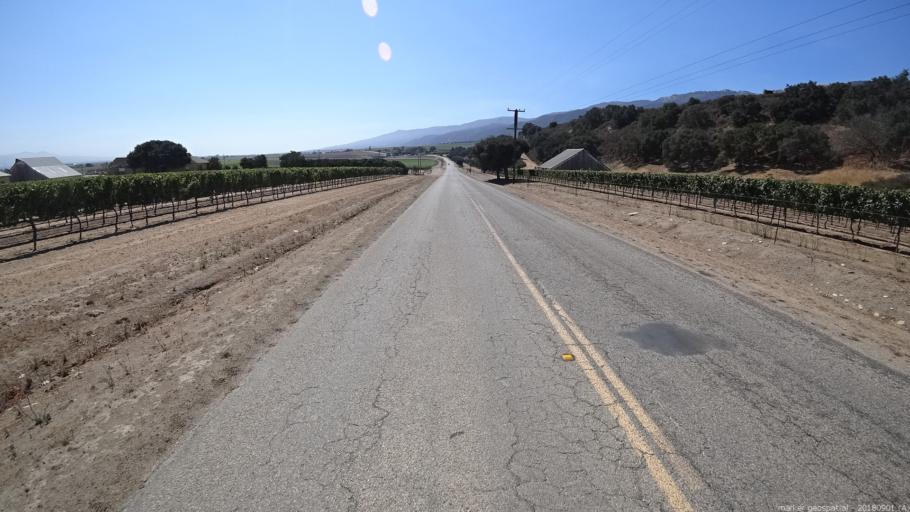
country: US
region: California
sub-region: Monterey County
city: Chualar
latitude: 36.5173
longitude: -121.5199
